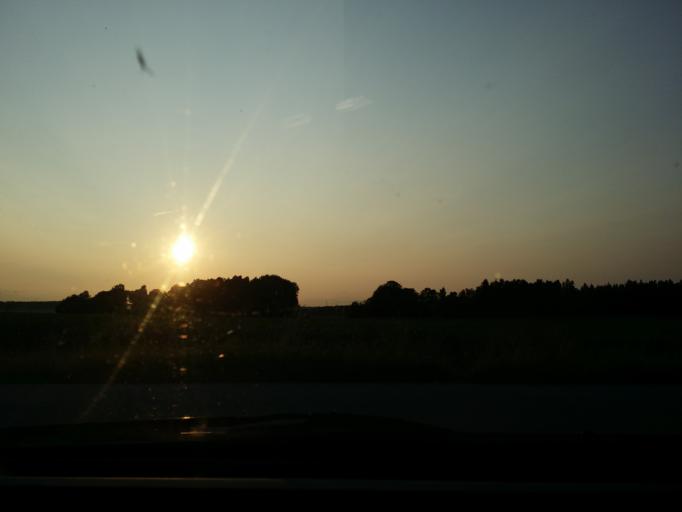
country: SE
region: Vaestmanland
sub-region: Vasteras
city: Tillberga
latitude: 59.5784
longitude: 16.6827
